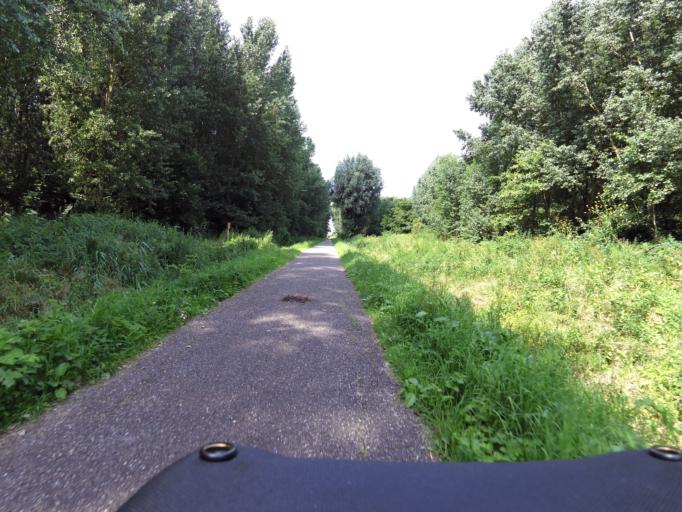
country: NL
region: South Holland
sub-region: Gemeente Albrandswaard
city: Rhoon
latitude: 51.8648
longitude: 4.3888
